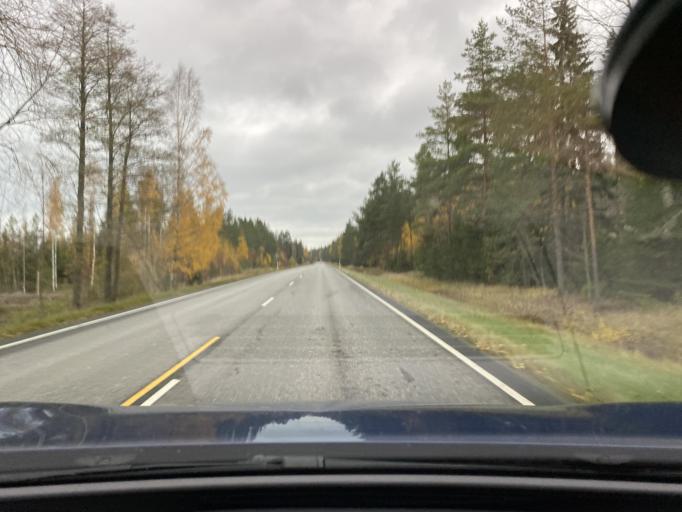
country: FI
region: Varsinais-Suomi
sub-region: Loimaa
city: Ylaene
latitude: 60.9120
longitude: 22.4135
